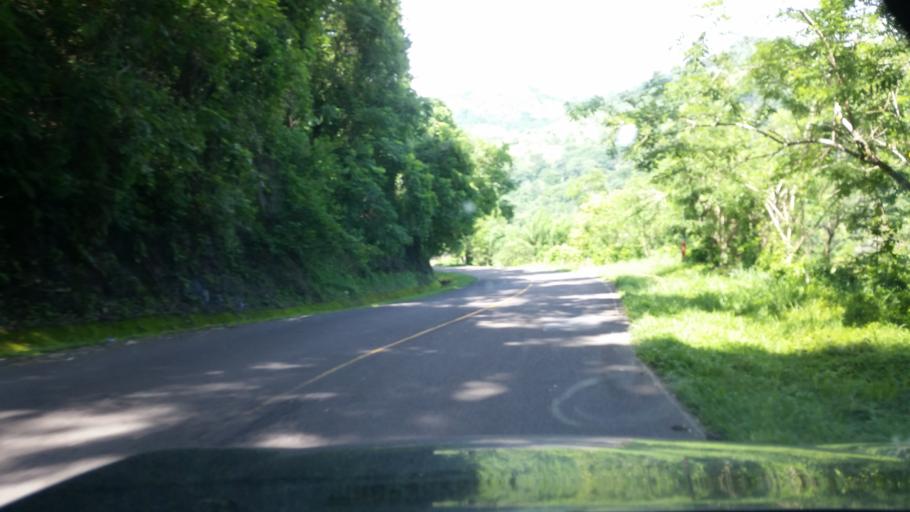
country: NI
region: Matagalpa
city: San Ramon
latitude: 13.0233
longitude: -85.7862
